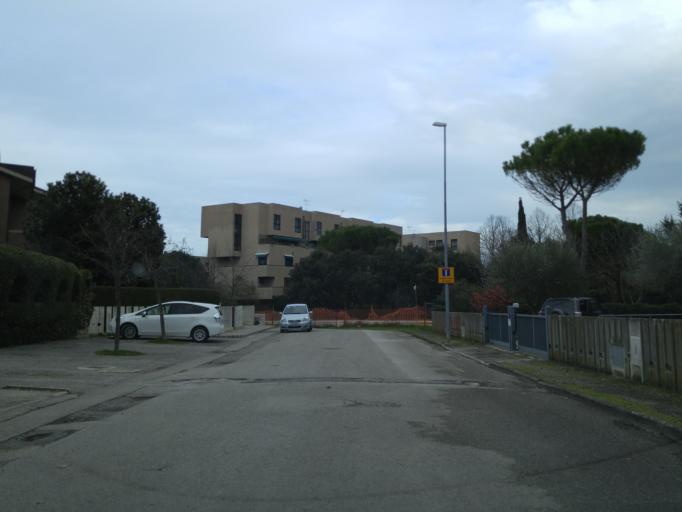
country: IT
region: The Marches
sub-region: Provincia di Pesaro e Urbino
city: Fano
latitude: 43.8410
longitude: 13.0015
